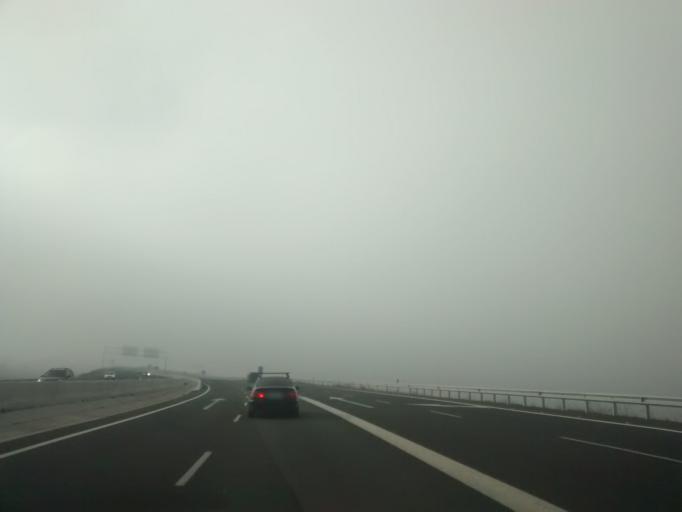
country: ES
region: La Rioja
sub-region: Provincia de La Rioja
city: Villamediana de Iregua
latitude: 42.4605
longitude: -2.3760
